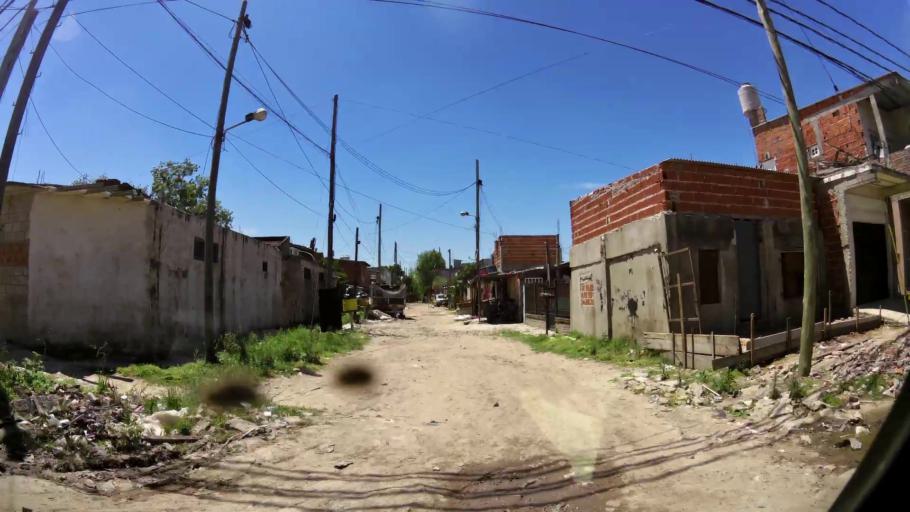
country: AR
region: Buenos Aires
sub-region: Partido de Quilmes
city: Quilmes
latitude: -34.7223
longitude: -58.3188
